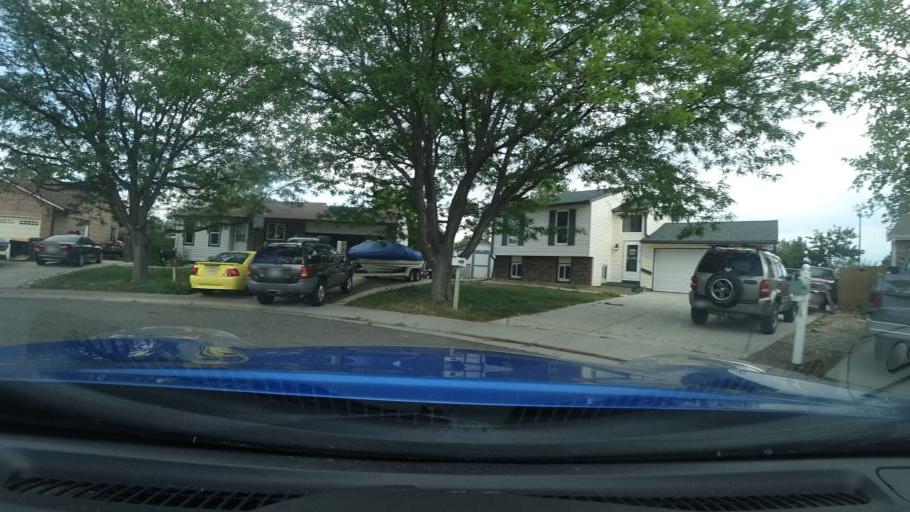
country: US
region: Colorado
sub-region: Adams County
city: Aurora
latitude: 39.6862
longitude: -104.7933
